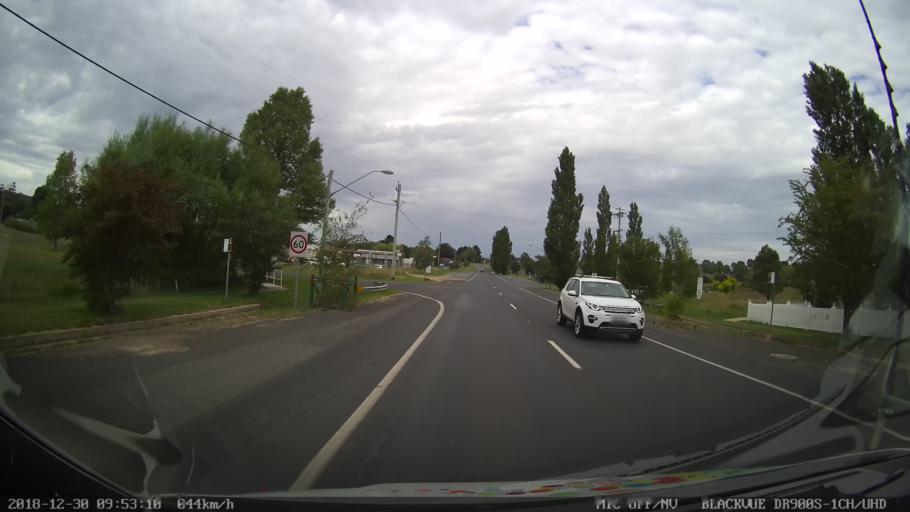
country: AU
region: New South Wales
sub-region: Cooma-Monaro
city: Cooma
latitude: -36.5138
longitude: 149.2834
